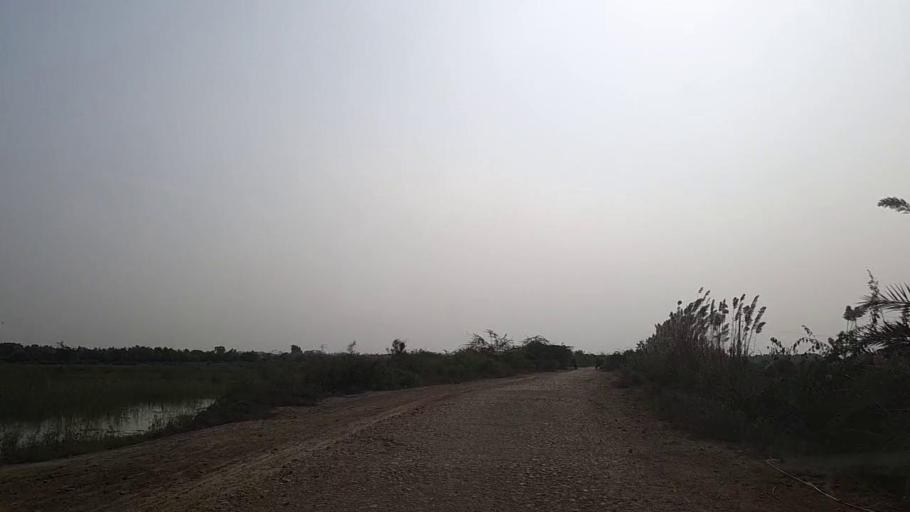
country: PK
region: Sindh
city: Gharo
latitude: 24.6487
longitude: 67.6182
